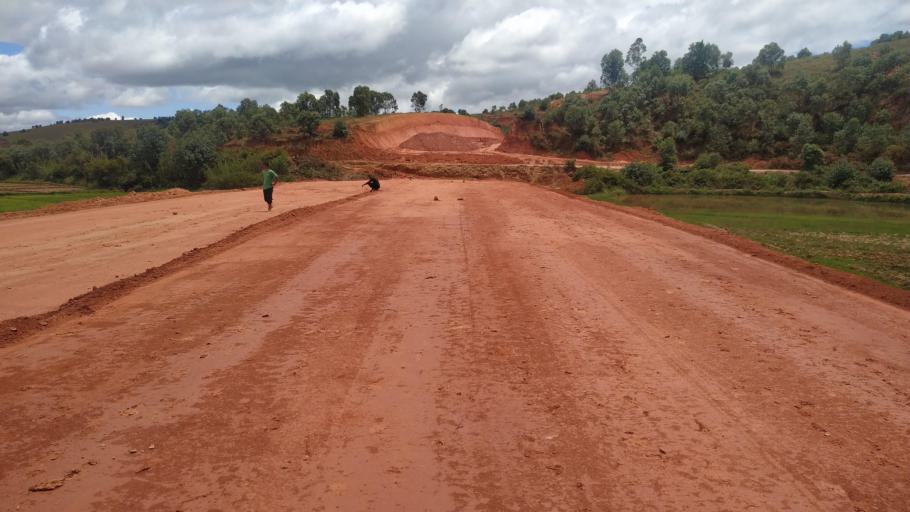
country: MG
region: Alaotra Mangoro
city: Ambatondrazaka
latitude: -18.0007
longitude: 48.2626
